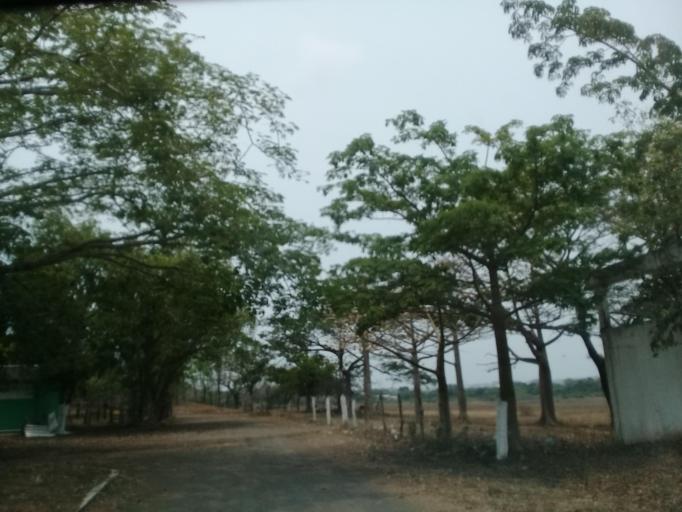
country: MX
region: Veracruz
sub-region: Veracruz
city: Lomas de Rio Medio Cuatro
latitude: 19.1714
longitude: -96.2103
